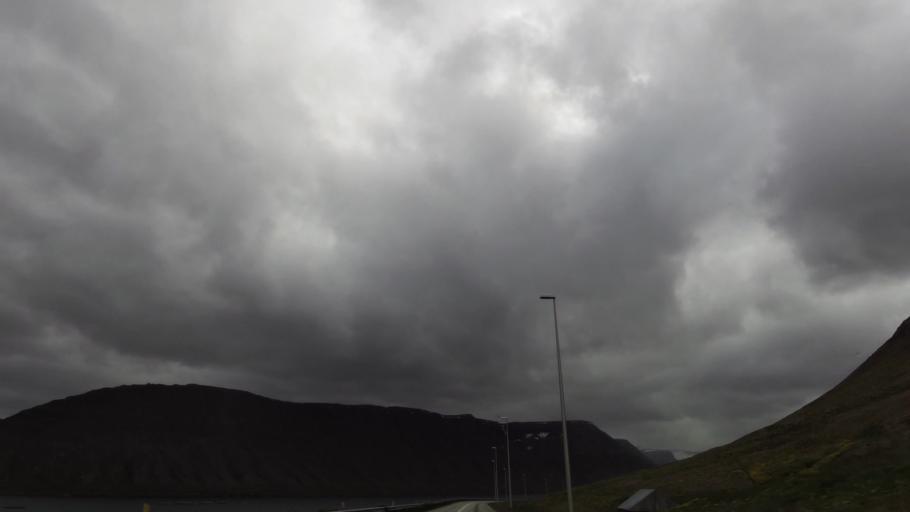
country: IS
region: Westfjords
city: Isafjoerdur
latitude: 66.1015
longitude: -23.1093
